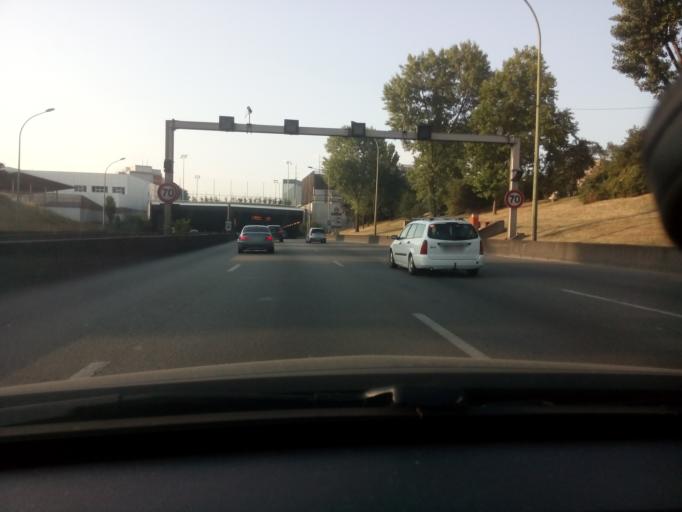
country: FR
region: Ile-de-France
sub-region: Departement de Seine-Saint-Denis
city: Le Pre-Saint-Gervais
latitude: 48.8758
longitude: 2.4096
